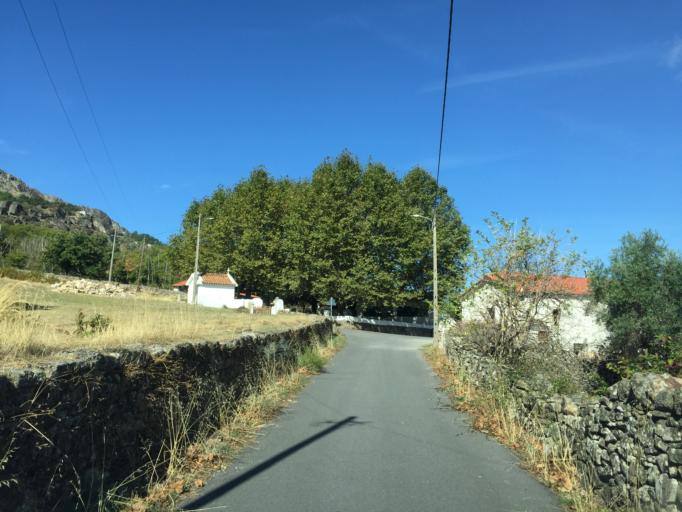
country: PT
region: Portalegre
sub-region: Marvao
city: Marvao
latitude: 39.3982
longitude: -7.3687
